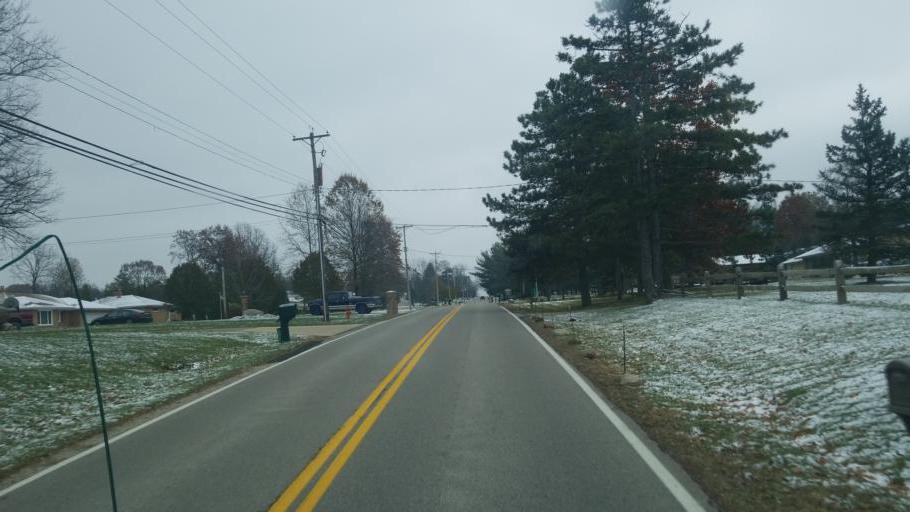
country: US
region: Ohio
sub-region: Cuyahoga County
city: North Royalton
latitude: 41.2807
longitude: -81.7199
